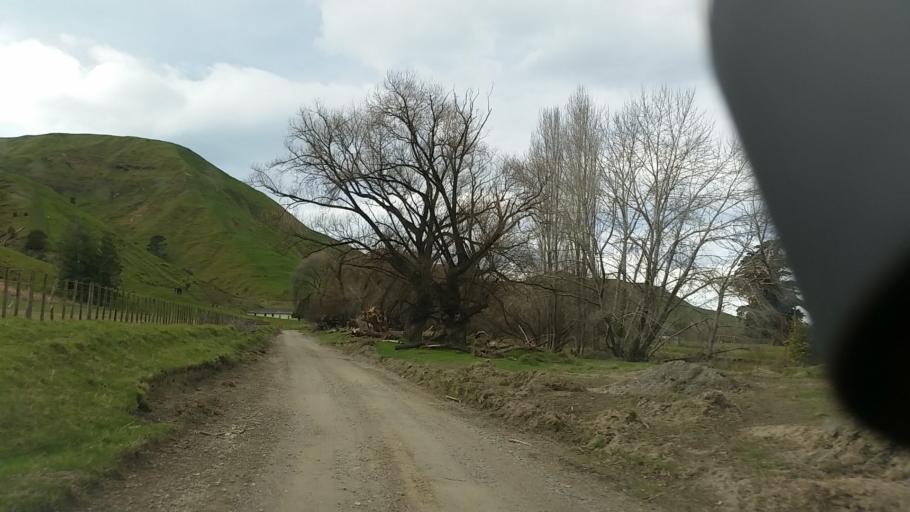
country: NZ
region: Hawke's Bay
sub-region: Napier City
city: Napier
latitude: -39.2696
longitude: 176.9796
